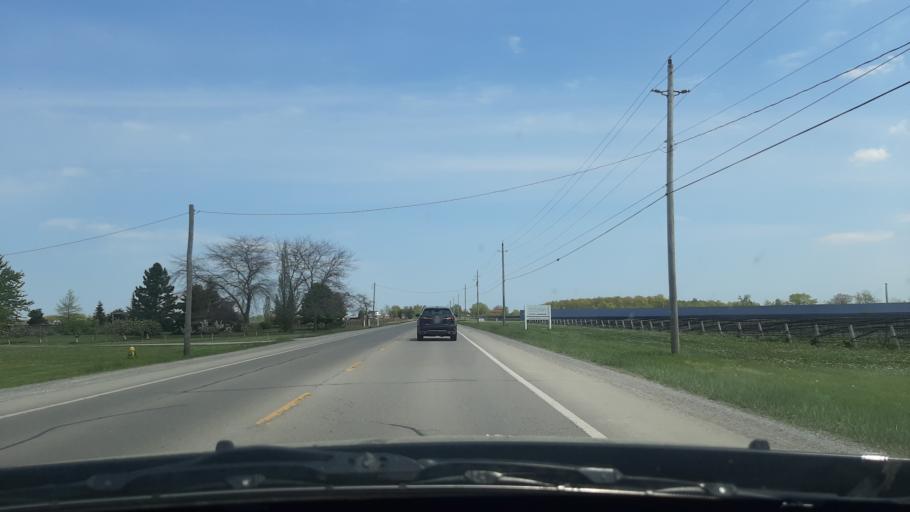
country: CA
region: Ontario
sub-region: Regional Municipality of Niagara
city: St. Catharines
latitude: 43.1900
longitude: -79.1636
